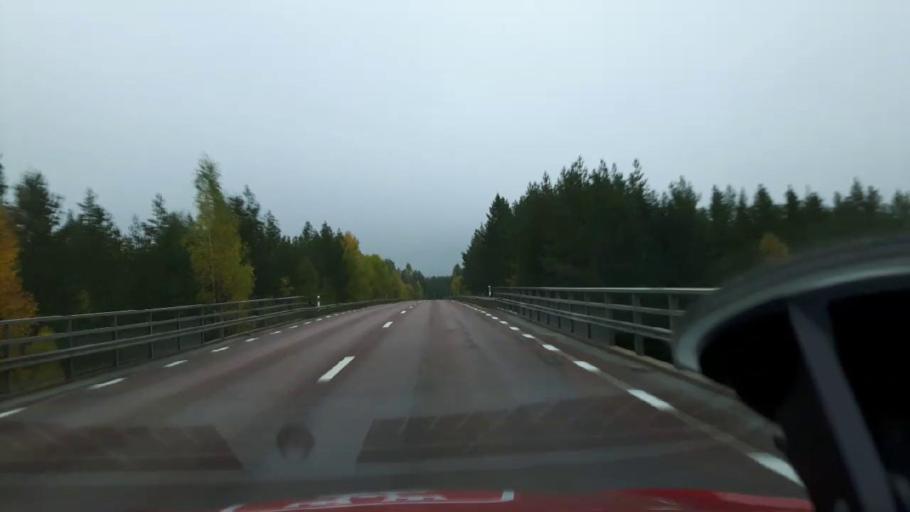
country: SE
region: Jaemtland
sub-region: Bergs Kommun
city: Hoverberg
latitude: 62.6159
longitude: 14.3852
